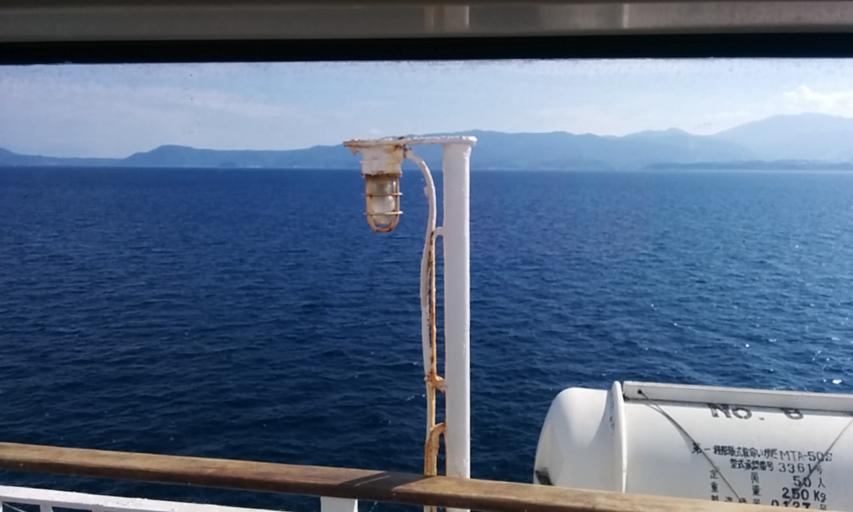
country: JP
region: Kagoshima
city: Tarumizu
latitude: 31.4667
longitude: 130.6261
